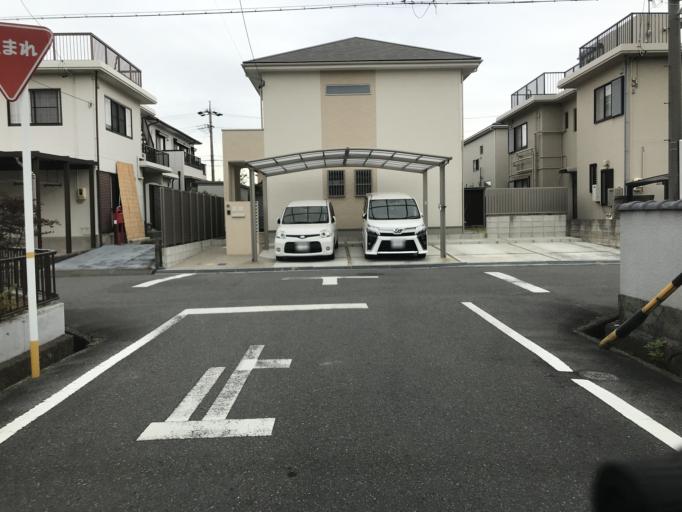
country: JP
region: Aichi
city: Kanie
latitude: 35.1769
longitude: 136.7791
